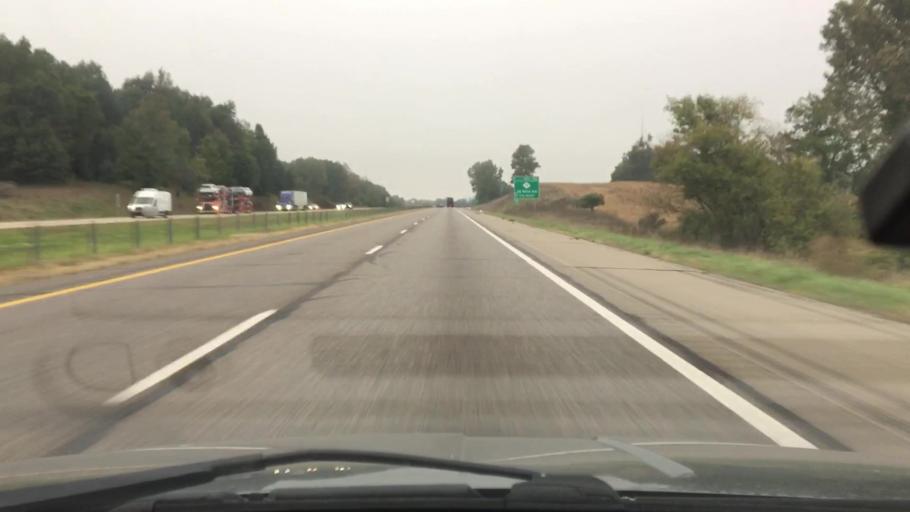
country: US
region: Michigan
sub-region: Calhoun County
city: Albion
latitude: 42.2731
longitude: -84.7816
